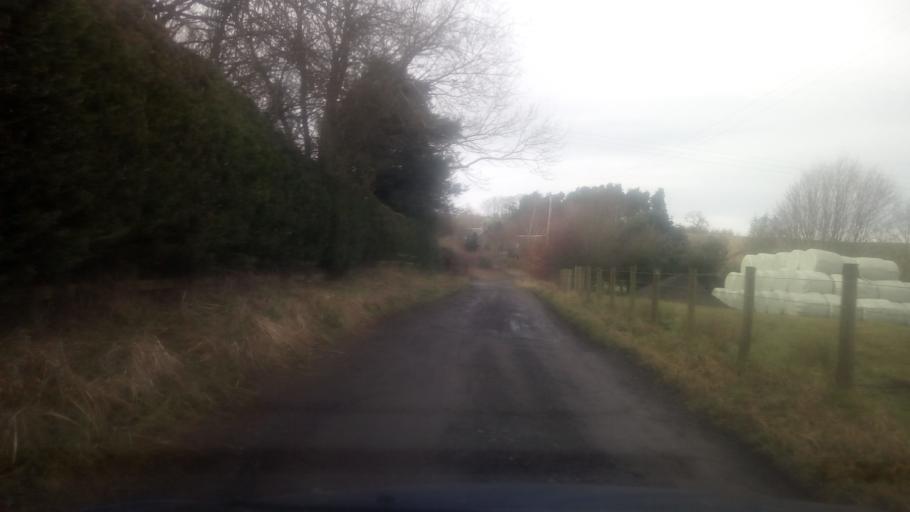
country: GB
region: Scotland
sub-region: The Scottish Borders
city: Jedburgh
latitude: 55.4607
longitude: -2.5661
